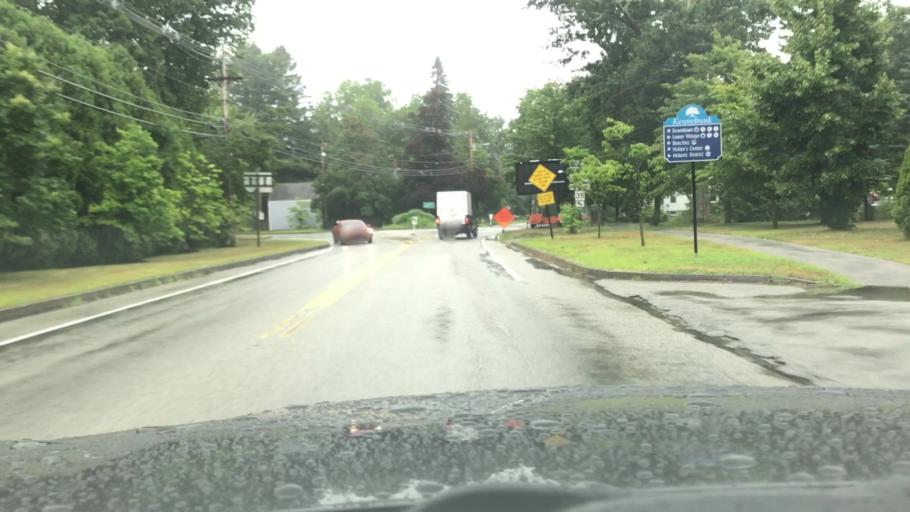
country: US
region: Maine
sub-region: York County
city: Kennebunk
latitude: 43.3913
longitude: -70.5460
